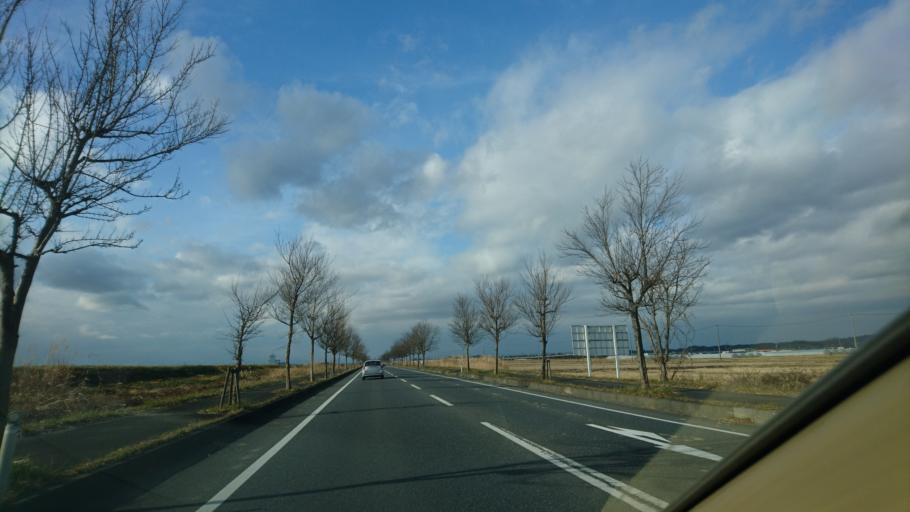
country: JP
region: Miyagi
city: Wakuya
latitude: 38.5381
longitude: 141.1164
